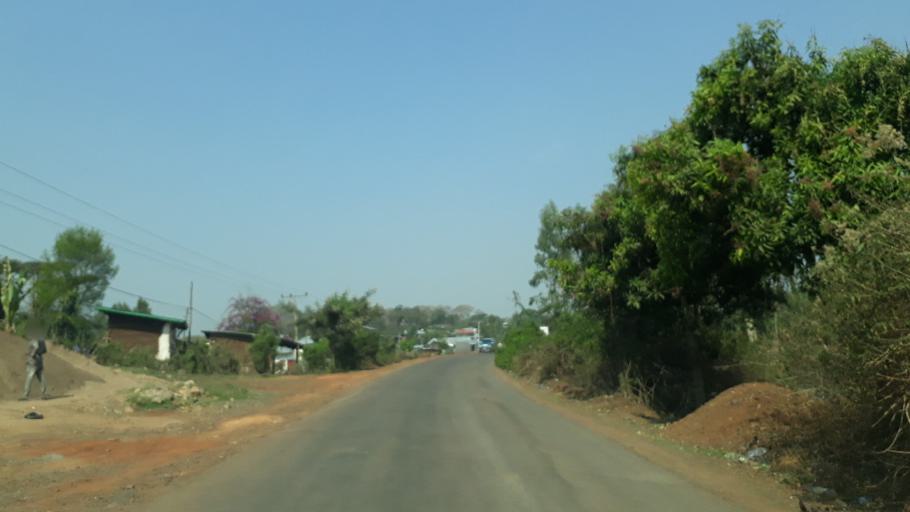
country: ET
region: Oromiya
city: Agaro
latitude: 7.8525
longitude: 36.6149
